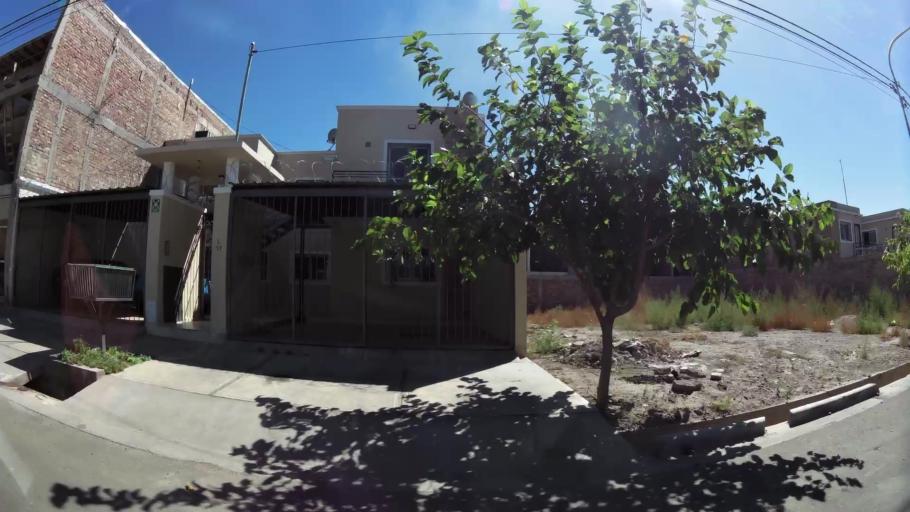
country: AR
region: Mendoza
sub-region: Departamento de Godoy Cruz
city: Godoy Cruz
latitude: -32.9660
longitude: -68.8426
